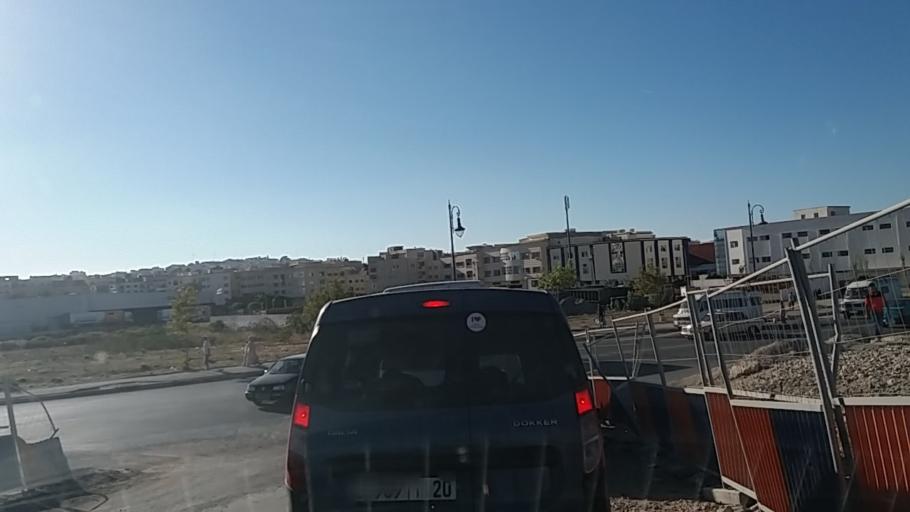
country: MA
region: Tanger-Tetouan
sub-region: Tanger-Assilah
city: Tangier
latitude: 35.7353
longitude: -5.7960
